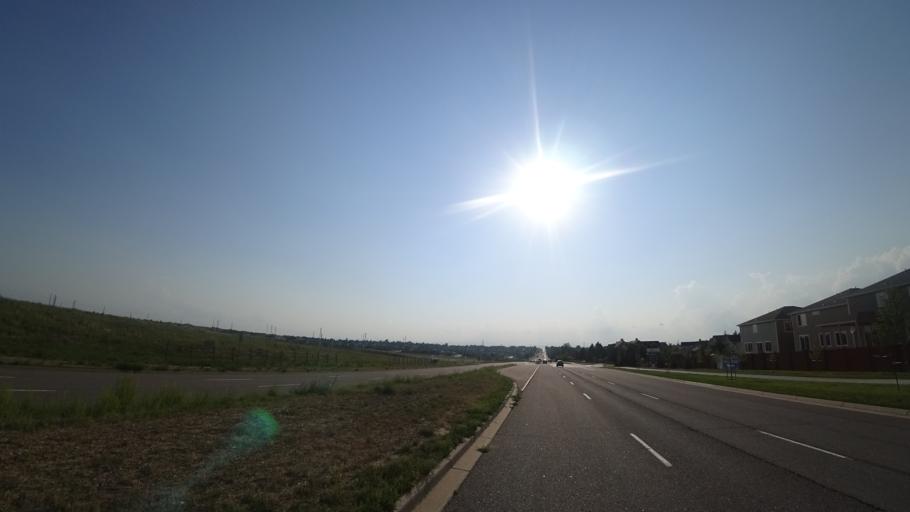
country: US
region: Colorado
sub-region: Arapahoe County
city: Dove Valley
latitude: 39.6385
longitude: -104.7402
